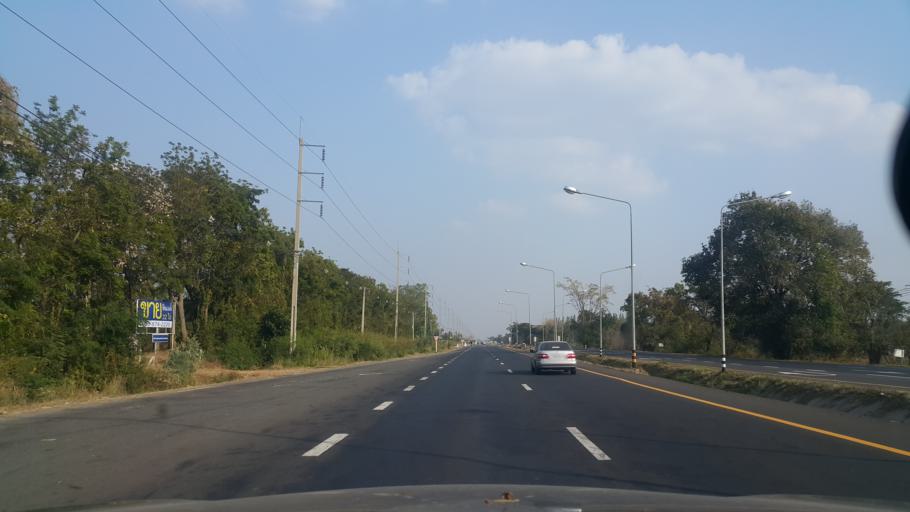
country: TH
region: Buriram
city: Chaloem Phra Kiat
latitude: 14.6179
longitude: 102.8980
